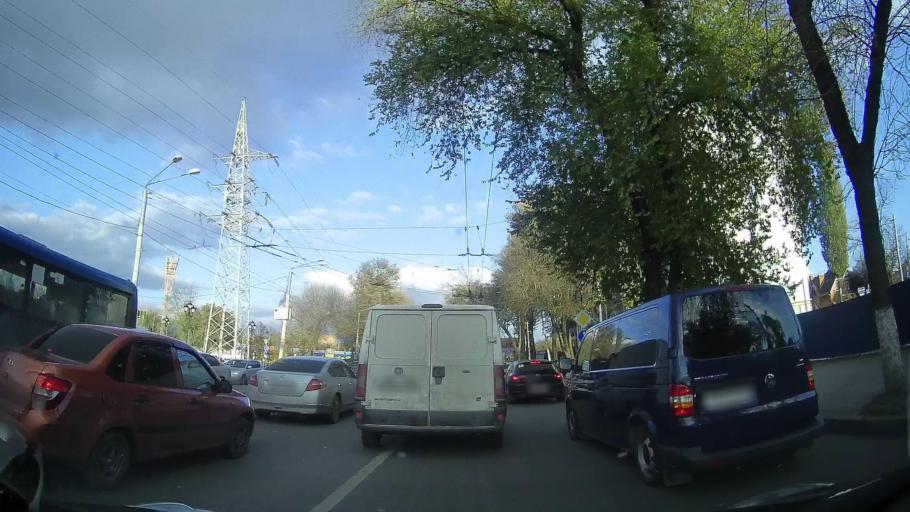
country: RU
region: Rostov
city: Rostov-na-Donu
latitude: 47.2410
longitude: 39.7586
